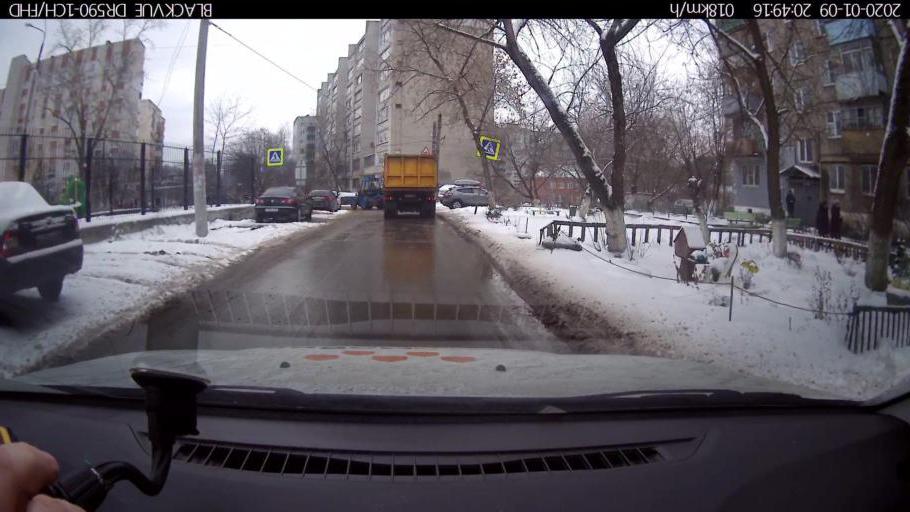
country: RU
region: Nizjnij Novgorod
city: Nizhniy Novgorod
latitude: 56.2913
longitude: 43.9390
